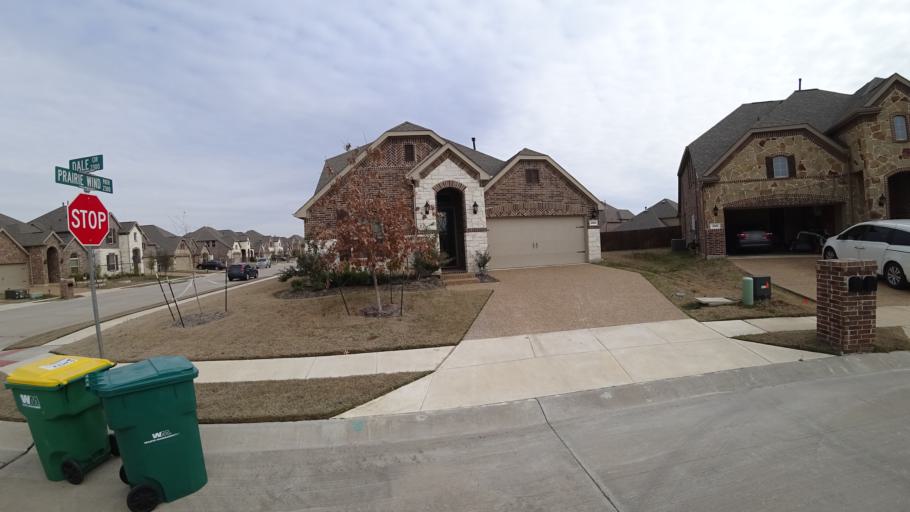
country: US
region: Texas
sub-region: Denton County
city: The Colony
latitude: 33.0500
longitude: -96.9152
